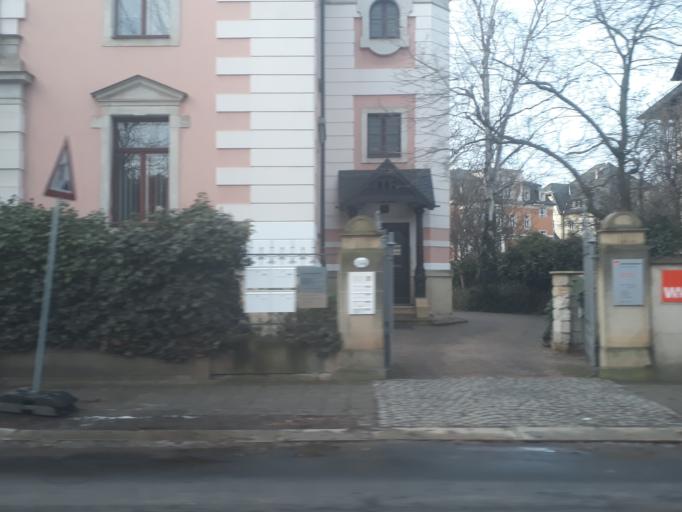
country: DE
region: Saxony
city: Dresden
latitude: 51.0291
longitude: 13.7587
